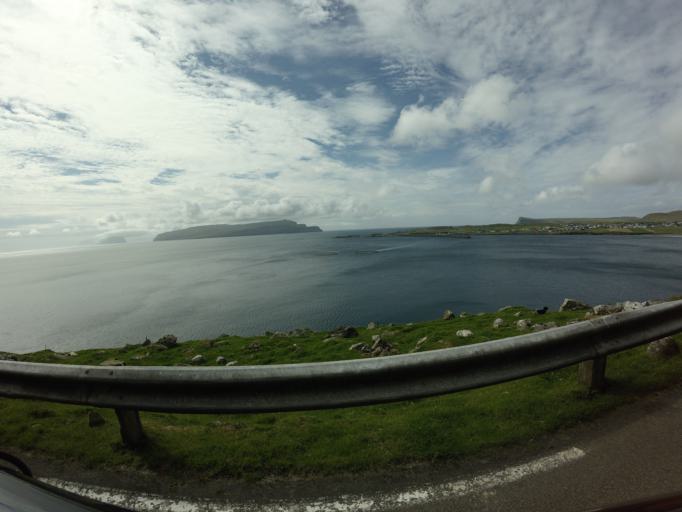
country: FO
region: Sandoy
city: Sandur
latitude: 61.8348
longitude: -6.7893
